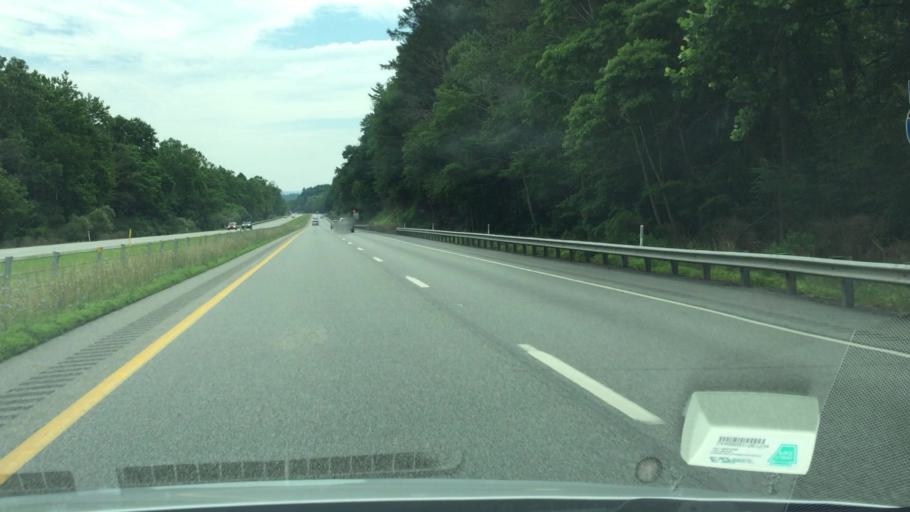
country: US
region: Maryland
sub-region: Washington County
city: Hancock
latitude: 39.7980
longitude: -78.2400
